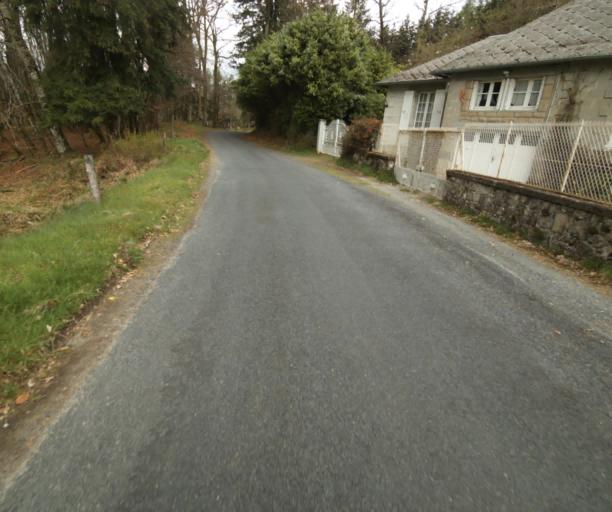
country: FR
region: Limousin
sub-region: Departement de la Correze
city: Correze
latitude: 45.3553
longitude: 1.9318
